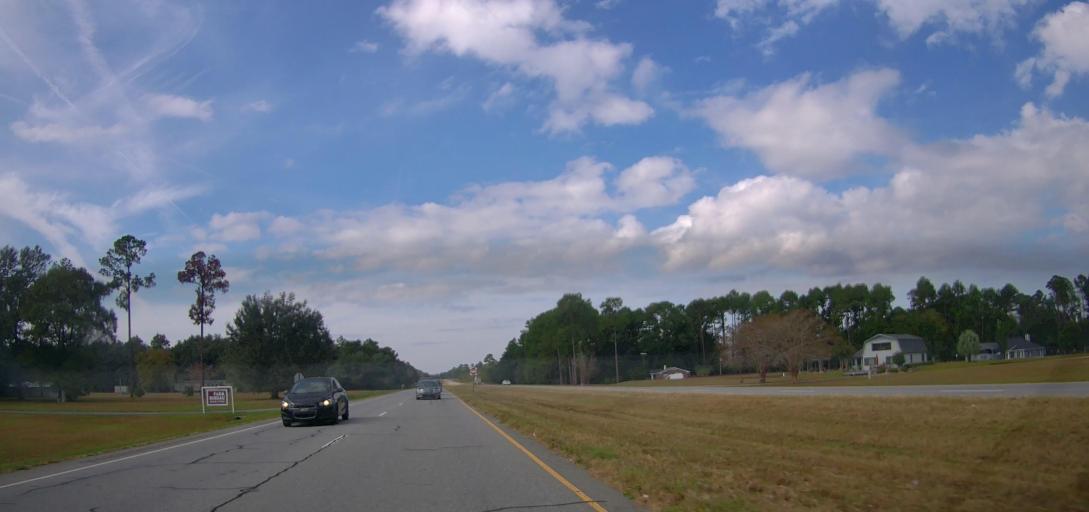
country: US
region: Georgia
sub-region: Mitchell County
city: Camilla
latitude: 31.2039
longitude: -84.1723
